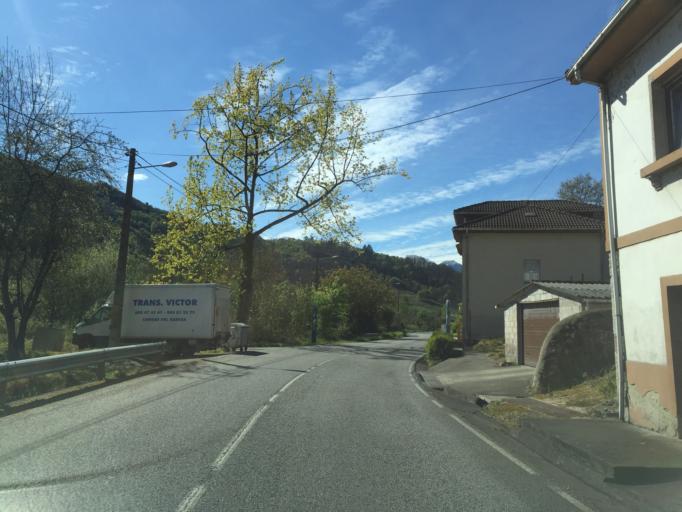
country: ES
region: Asturias
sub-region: Province of Asturias
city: Proaza
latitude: 43.3305
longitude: -5.9880
